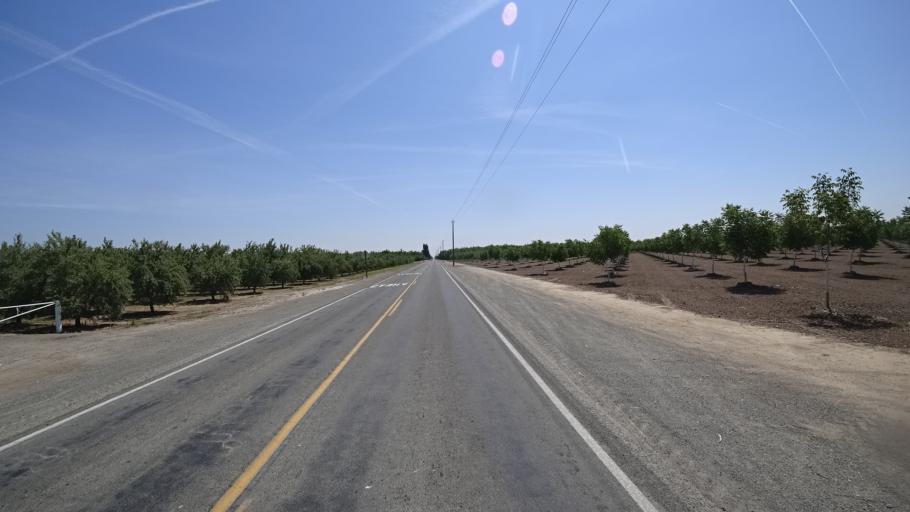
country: US
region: California
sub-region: Kings County
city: Lucerne
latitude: 36.4012
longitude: -119.6357
